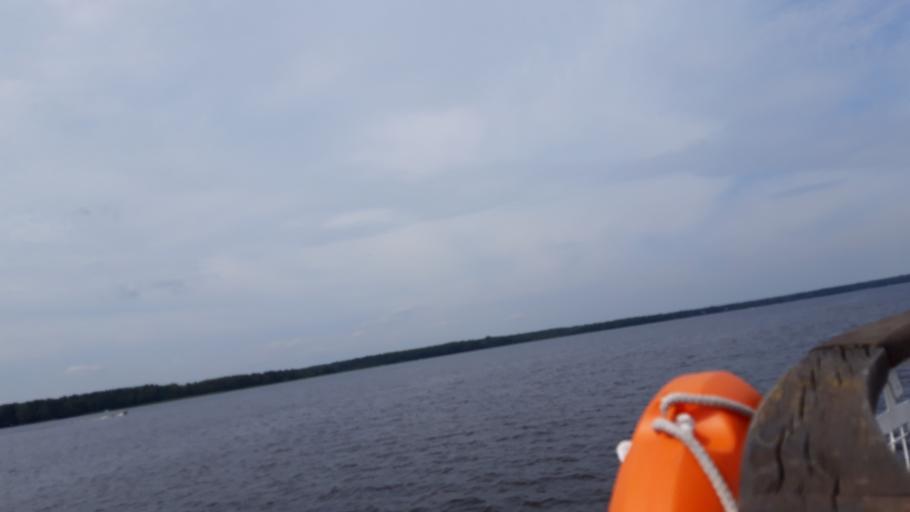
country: RU
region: Tverskaya
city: Konakovo
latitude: 56.7554
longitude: 36.7439
